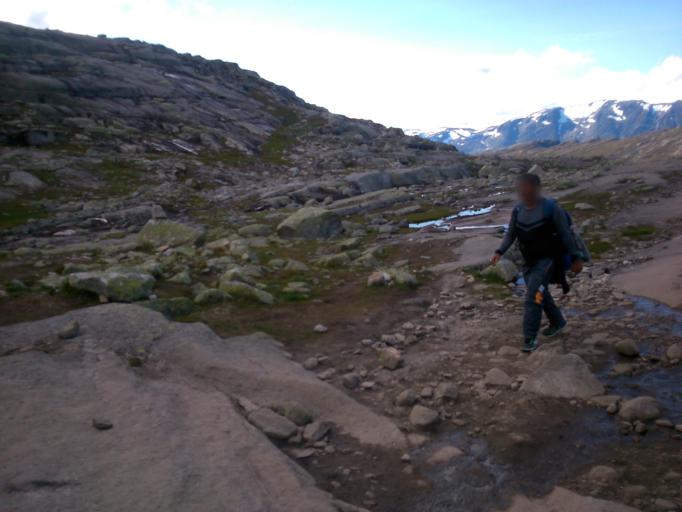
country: NO
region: Hordaland
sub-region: Odda
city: Odda
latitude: 60.1472
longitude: 6.6690
